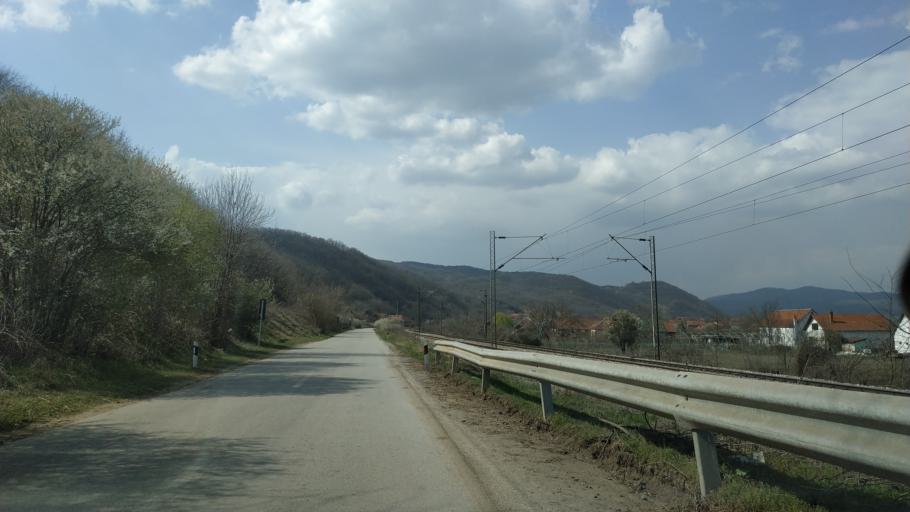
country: RS
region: Central Serbia
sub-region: Nisavski Okrug
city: Razanj
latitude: 43.5860
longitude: 21.5599
